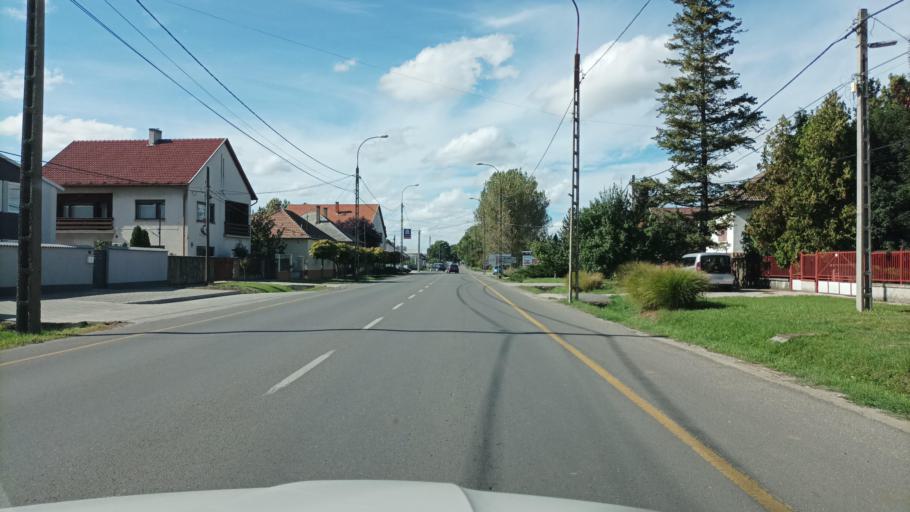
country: HU
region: Pest
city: Vecses
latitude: 47.4047
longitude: 19.2877
